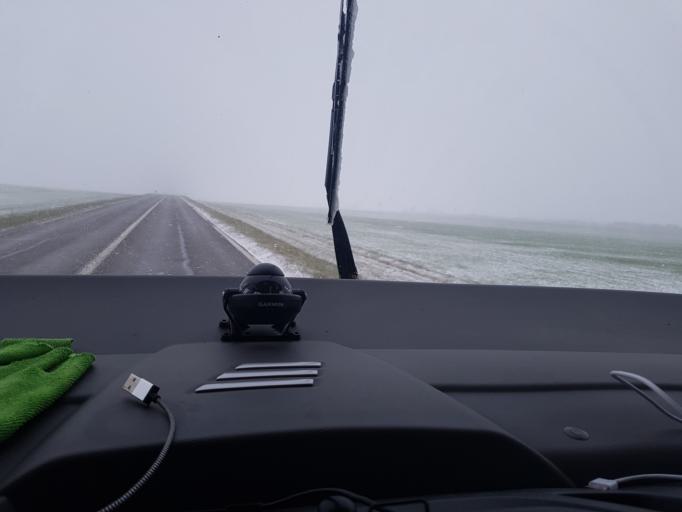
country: FR
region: Lorraine
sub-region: Departement de la Moselle
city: Chateau-Salins
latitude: 48.8770
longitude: 6.4103
